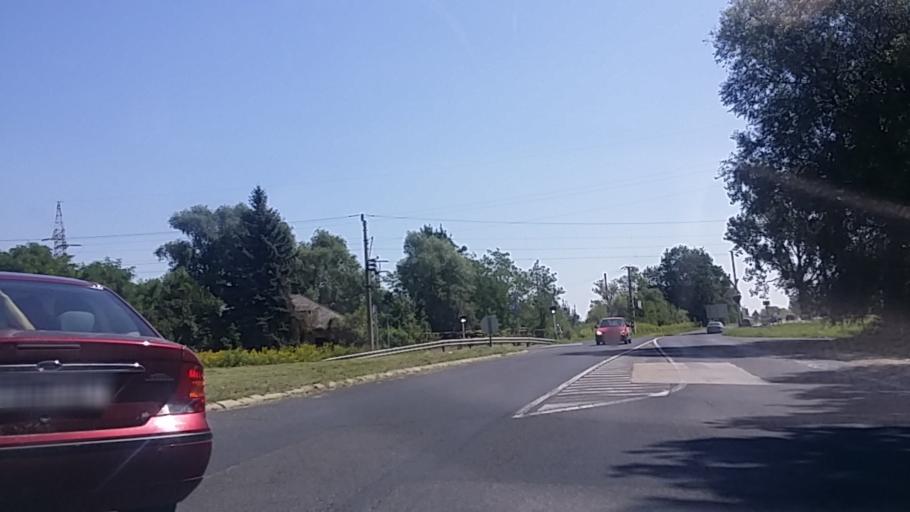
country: HU
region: Somogy
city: Balatonbereny
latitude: 46.7032
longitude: 17.2547
